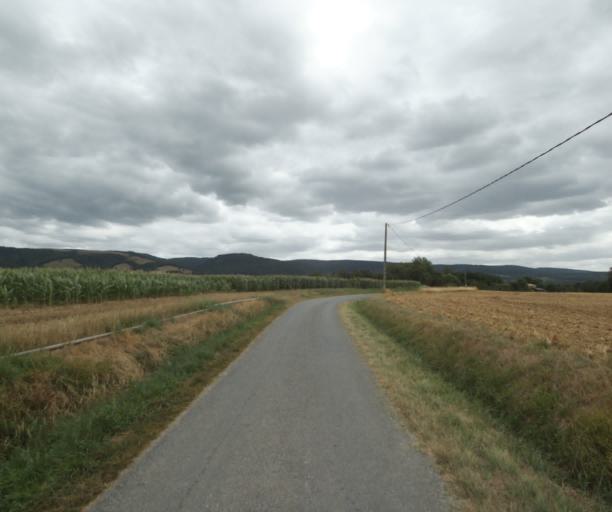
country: FR
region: Midi-Pyrenees
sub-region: Departement du Tarn
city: Soreze
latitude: 43.4710
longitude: 2.0667
